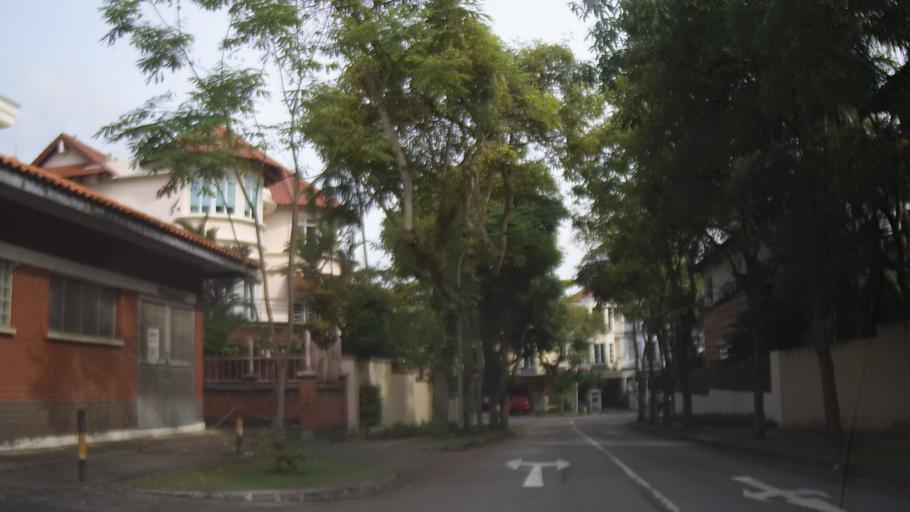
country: MY
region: Johor
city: Johor Bahru
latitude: 1.4277
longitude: 103.7801
